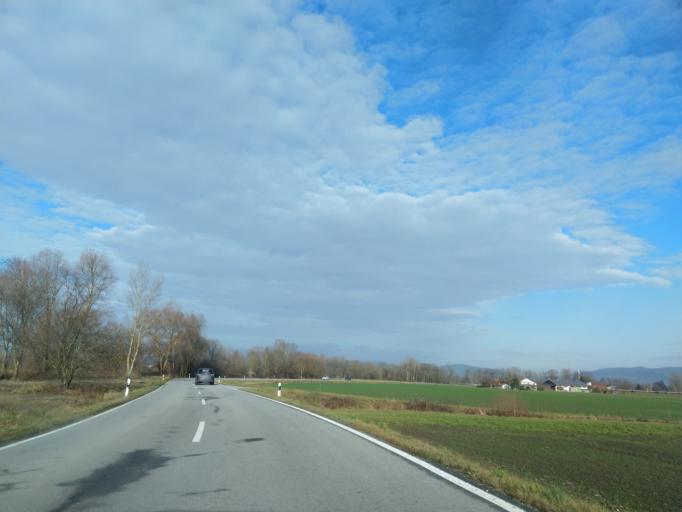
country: DE
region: Bavaria
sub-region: Lower Bavaria
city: Aholming
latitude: 48.7519
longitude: 12.9051
